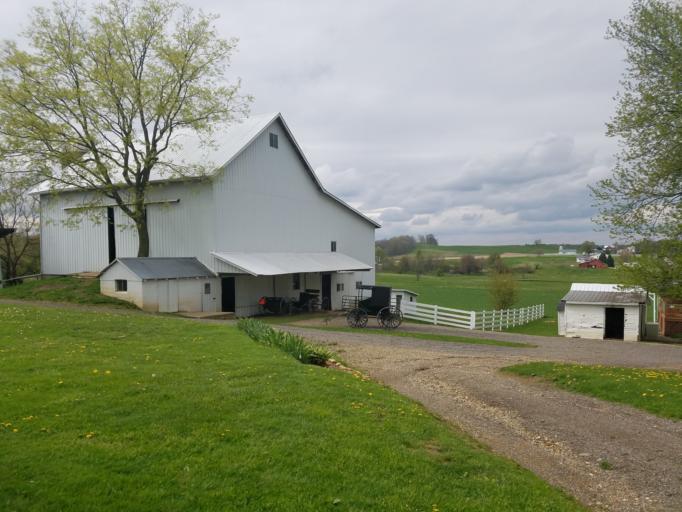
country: US
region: Ohio
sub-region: Knox County
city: Fredericktown
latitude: 40.5091
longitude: -82.6054
